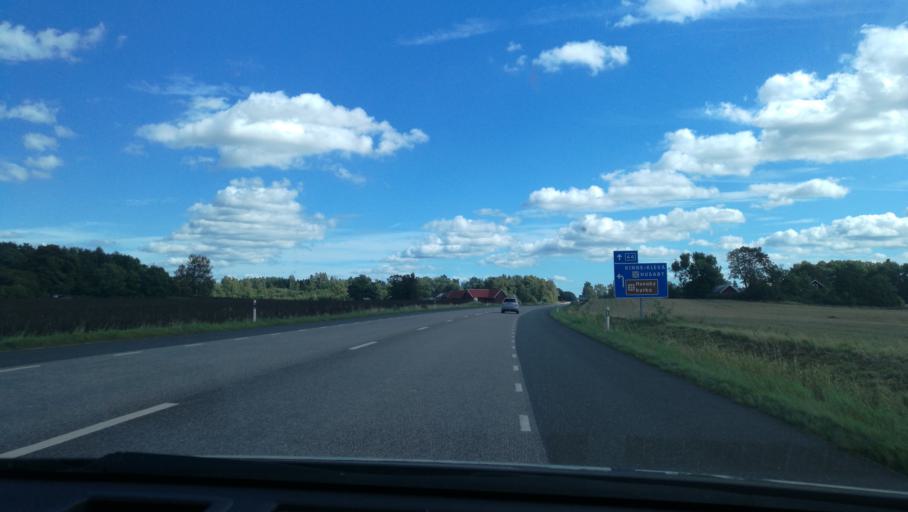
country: SE
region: Vaestra Goetaland
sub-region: Gotene Kommun
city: Kallby
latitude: 58.5116
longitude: 13.3393
